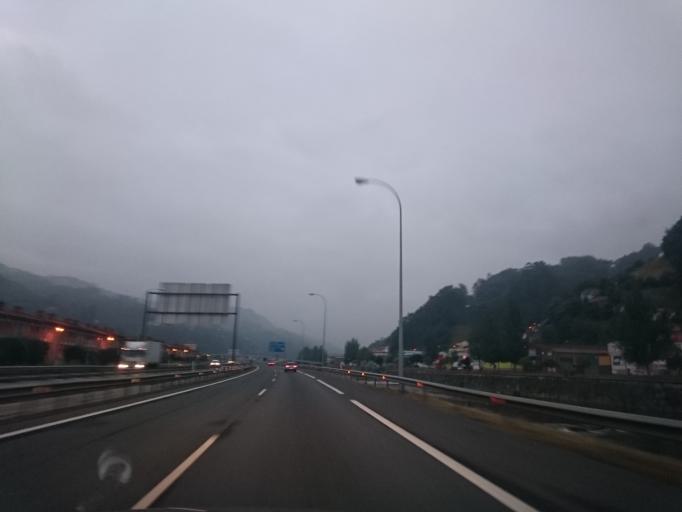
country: ES
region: Asturias
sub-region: Province of Asturias
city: Mieres
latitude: 43.2481
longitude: -5.7808
